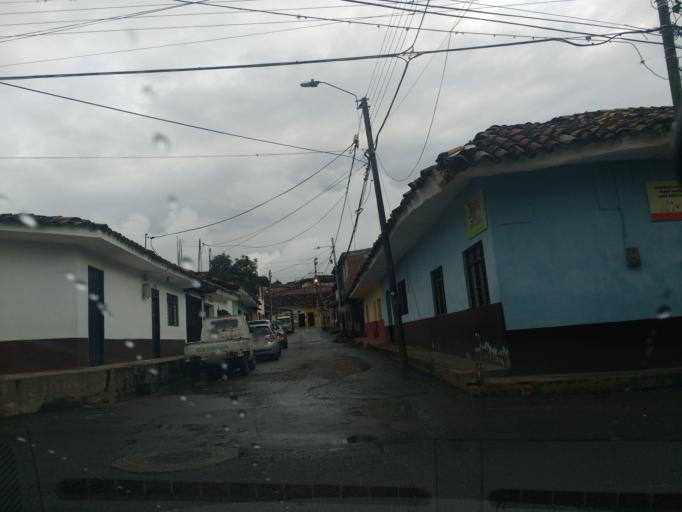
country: CO
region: Cauca
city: Santander de Quilichao
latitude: 3.0025
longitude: -76.4801
